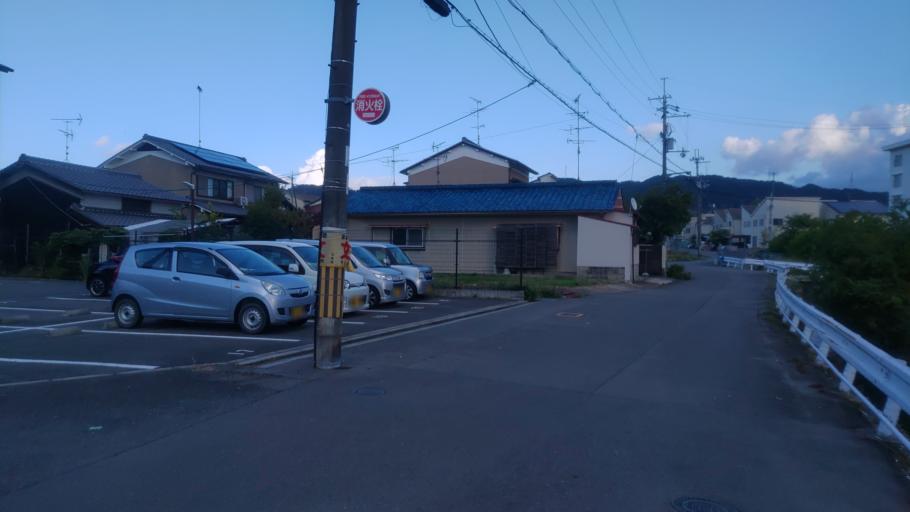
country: JP
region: Kyoto
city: Uji
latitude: 34.9149
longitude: 135.7954
